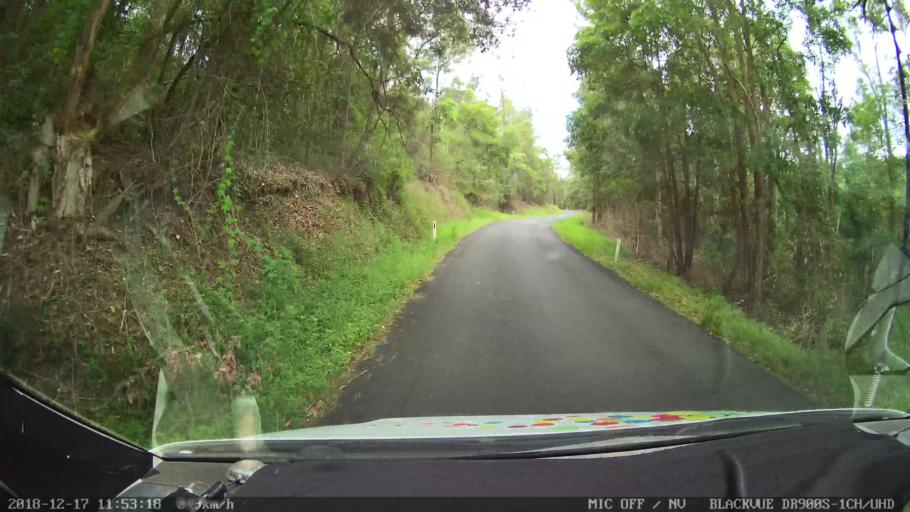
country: AU
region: New South Wales
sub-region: Kyogle
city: Kyogle
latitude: -28.5752
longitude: 152.5868
